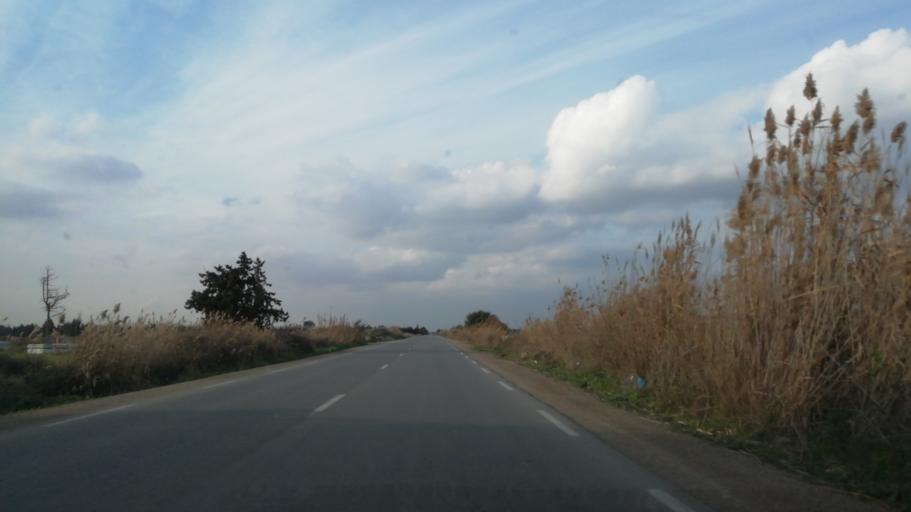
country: DZ
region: Mascara
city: Sig
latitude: 35.6389
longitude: 0.0334
